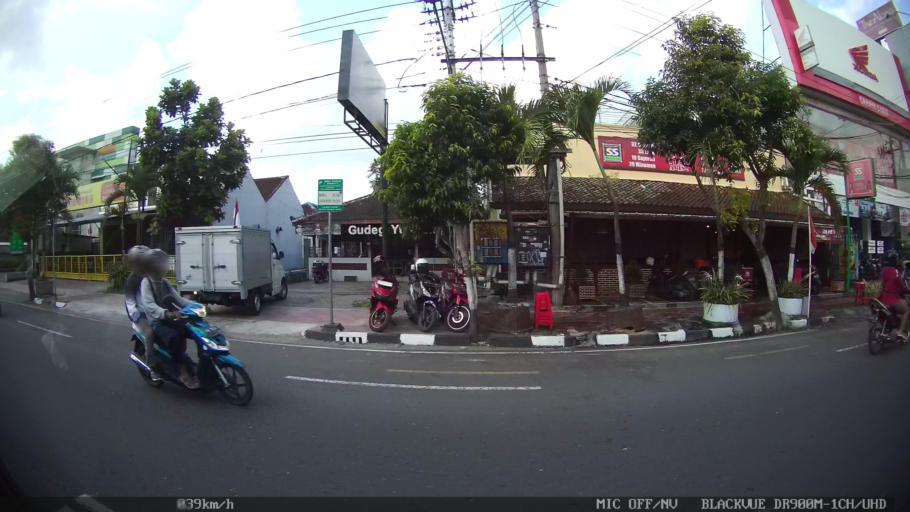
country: ID
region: Daerah Istimewa Yogyakarta
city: Yogyakarta
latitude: -7.8147
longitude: 110.3655
